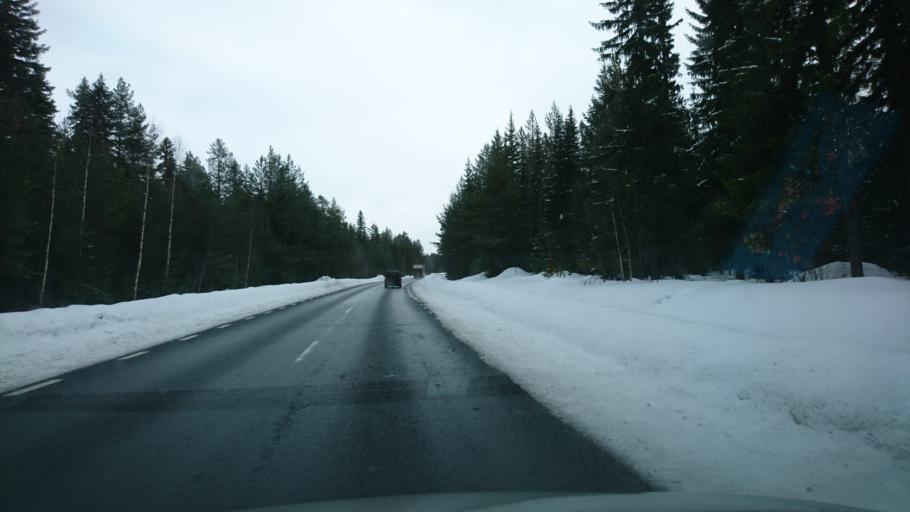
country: SE
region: Vaesternorrland
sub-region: Solleftea Kommun
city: Solleftea
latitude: 63.0346
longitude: 17.0874
